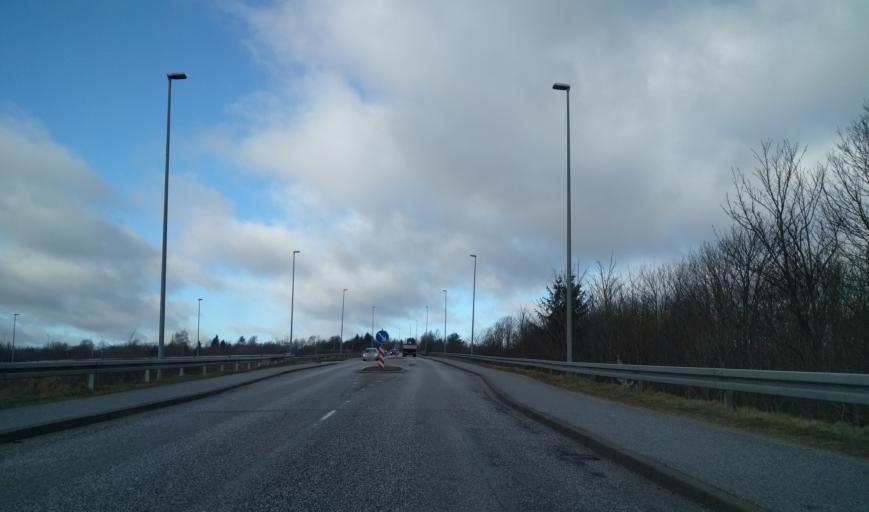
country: DK
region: North Denmark
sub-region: Alborg Kommune
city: Aalborg
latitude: 57.0113
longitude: 9.9078
